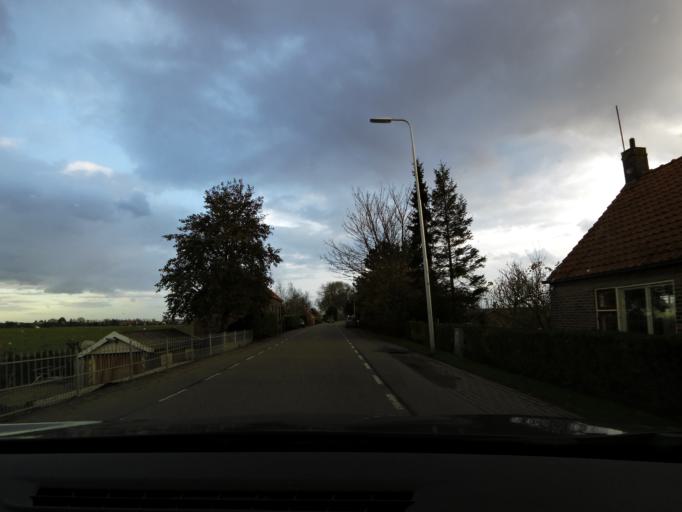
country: NL
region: South Holland
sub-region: Gemeente Binnenmaas
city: Mijnsheerenland
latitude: 51.8166
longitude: 4.5012
